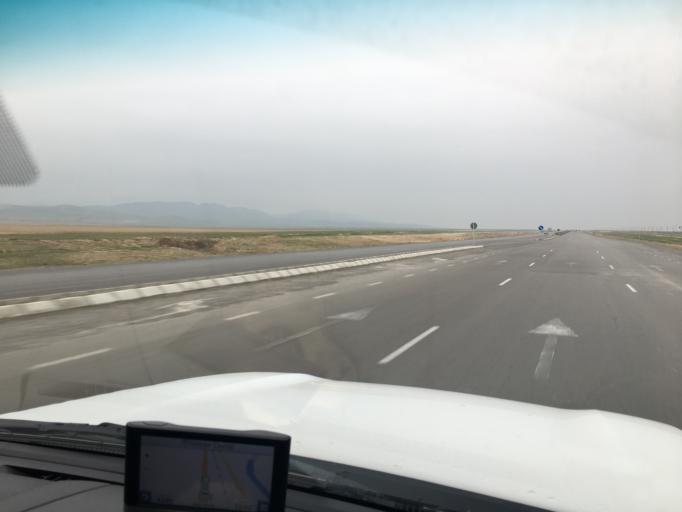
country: IR
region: Razavi Khorasan
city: Dargaz
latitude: 37.7427
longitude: 58.9733
